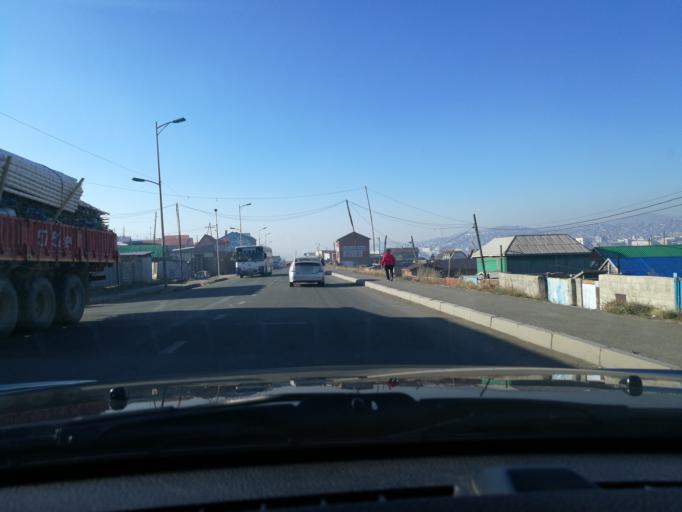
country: MN
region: Ulaanbaatar
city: Ulaanbaatar
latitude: 47.9748
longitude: 106.9327
